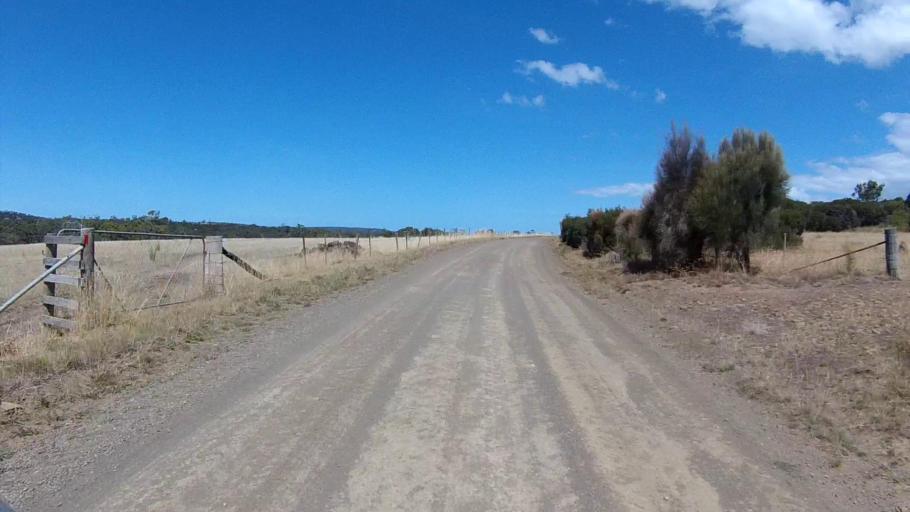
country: AU
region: Tasmania
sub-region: Break O'Day
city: St Helens
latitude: -41.9678
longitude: 148.0742
